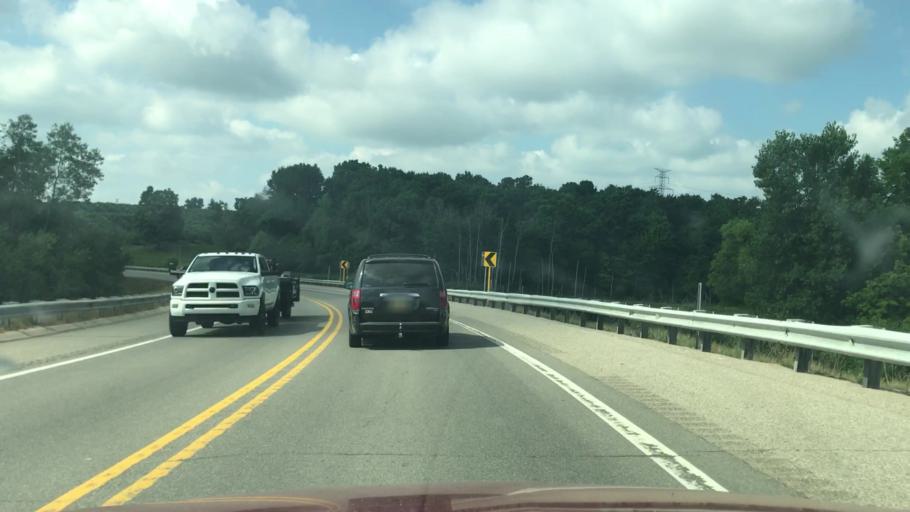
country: US
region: Michigan
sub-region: Kent County
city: Kent City
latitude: 43.2628
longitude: -85.8154
